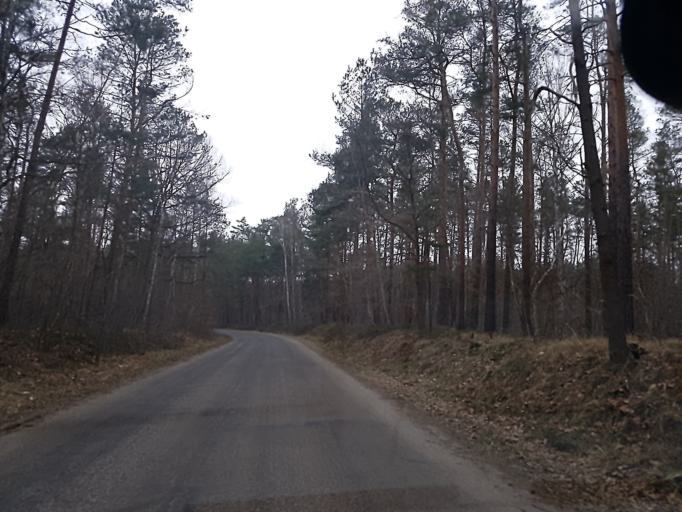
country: DE
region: Brandenburg
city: Ruckersdorf
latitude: 51.5962
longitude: 13.5656
